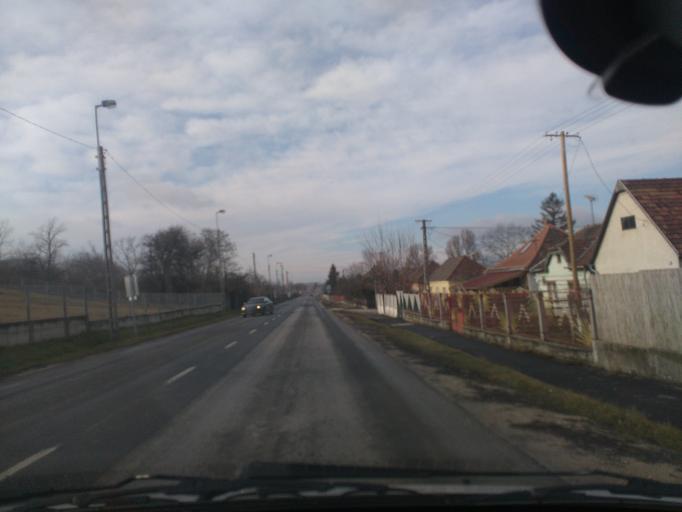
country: HU
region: Komarom-Esztergom
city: Tokod
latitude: 47.7333
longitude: 18.6854
